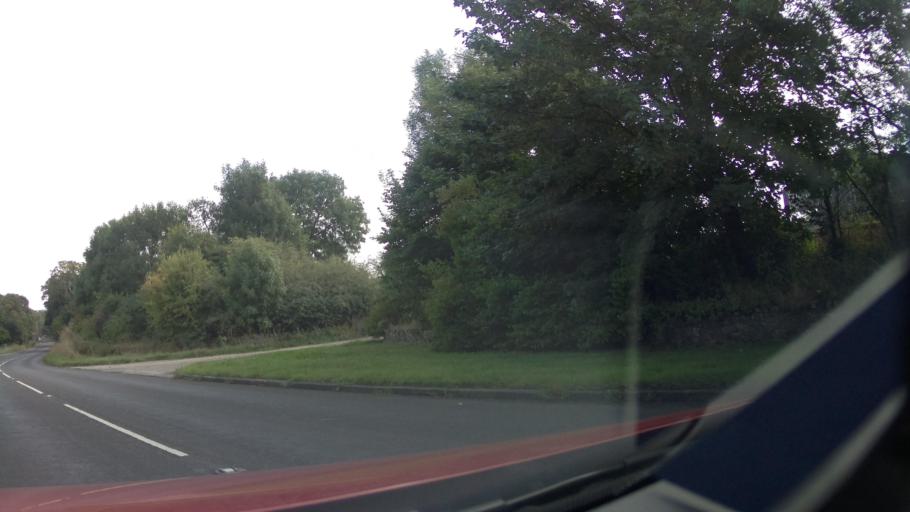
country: GB
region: England
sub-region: County Durham
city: High Etherley
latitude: 54.6345
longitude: -1.7338
